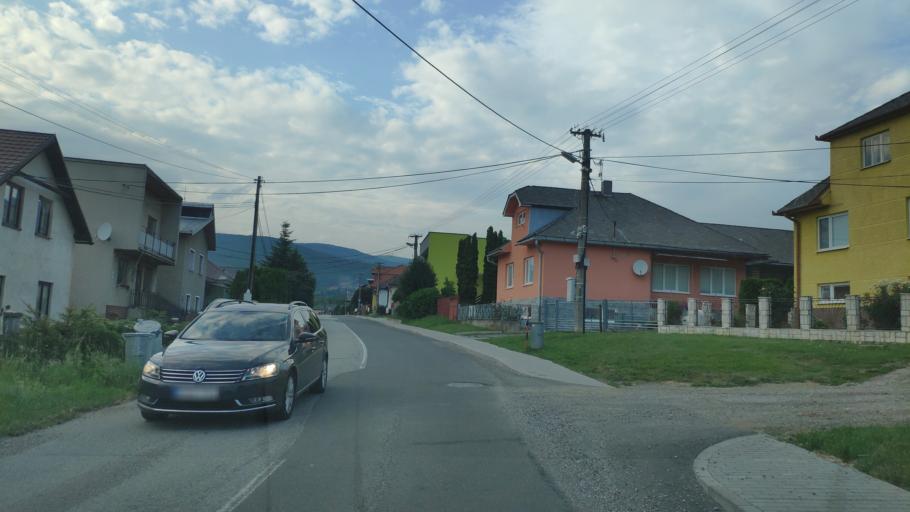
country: SK
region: Kosicky
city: Medzev
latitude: 48.7043
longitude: 20.9752
